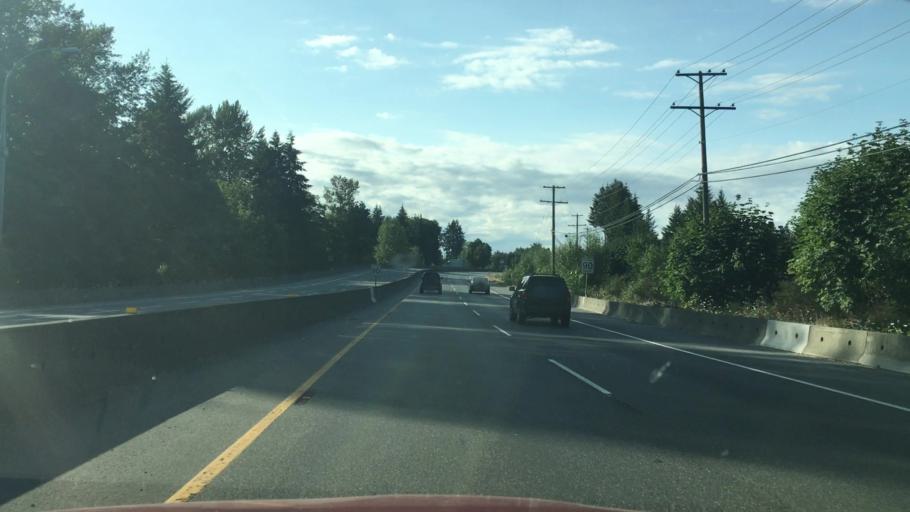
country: CA
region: British Columbia
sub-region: Cowichan Valley Regional District
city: Ladysmith
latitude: 49.0023
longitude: -123.8315
